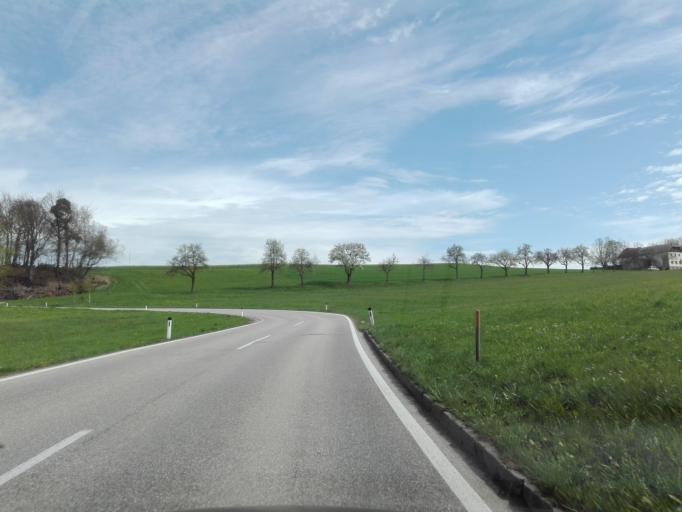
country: AT
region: Upper Austria
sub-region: Politischer Bezirk Urfahr-Umgebung
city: Eidenberg
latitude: 48.3563
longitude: 14.2393
